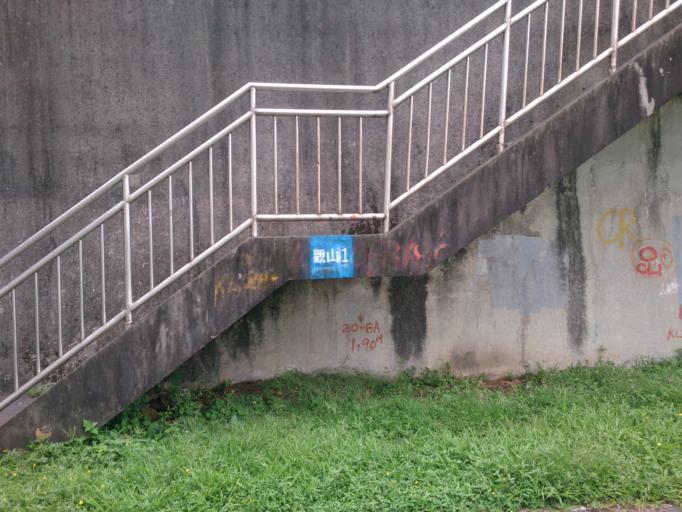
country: TW
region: Taipei
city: Taipei
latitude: 25.0551
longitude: 121.5703
